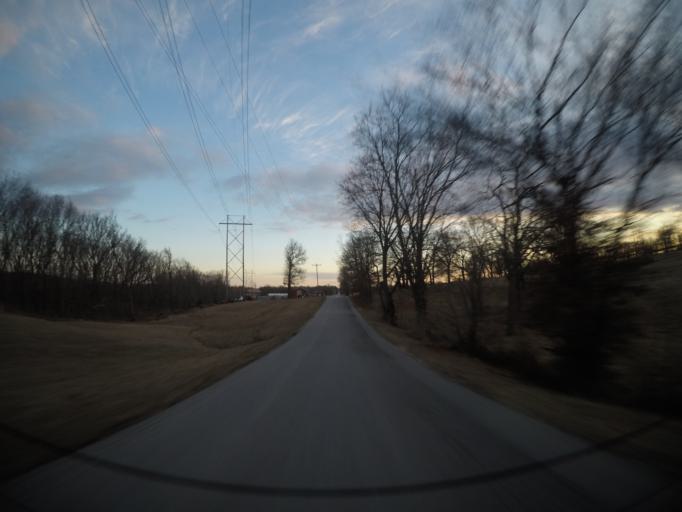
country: US
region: Kansas
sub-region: Wyandotte County
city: Bonner Springs
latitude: 39.0571
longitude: -94.9088
